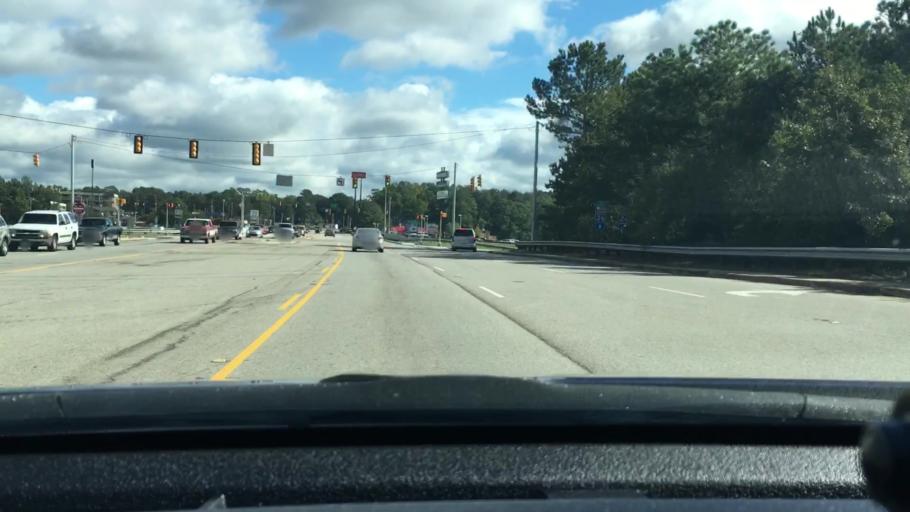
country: US
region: South Carolina
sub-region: Lexington County
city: Seven Oaks
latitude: 34.0668
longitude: -81.1439
